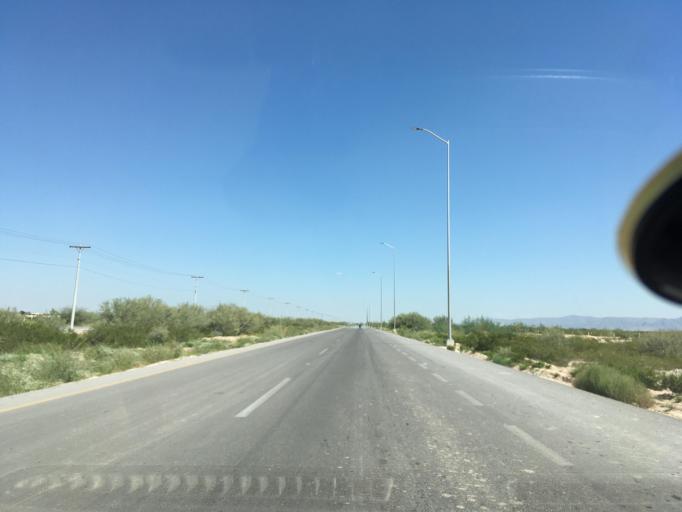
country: MX
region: Coahuila
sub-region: Torreon
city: Fraccionamiento la Noria
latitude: 25.4946
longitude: -103.3236
